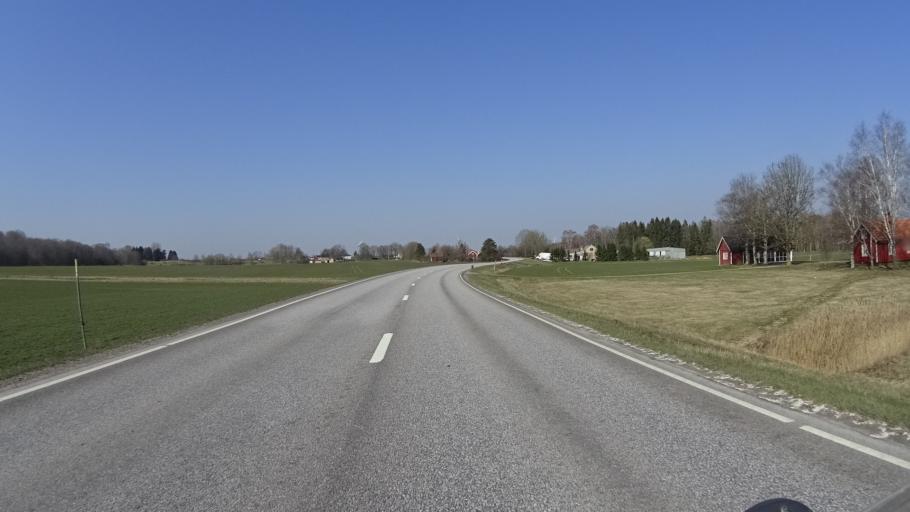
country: SE
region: OEstergoetland
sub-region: Mjolby Kommun
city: Mantorp
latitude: 58.3770
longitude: 15.2635
